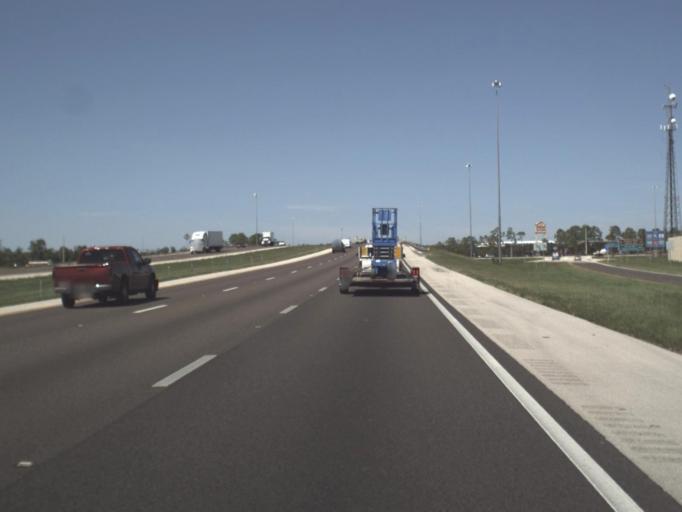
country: US
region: Florida
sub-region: Lee County
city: Estero
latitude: 26.4286
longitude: -81.7762
